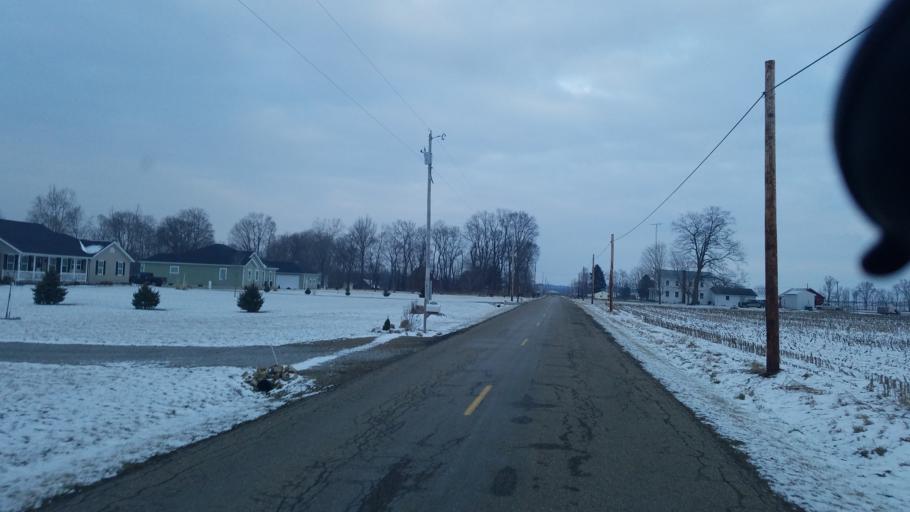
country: US
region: Ohio
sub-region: Knox County
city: Fredericktown
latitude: 40.4244
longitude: -82.5557
